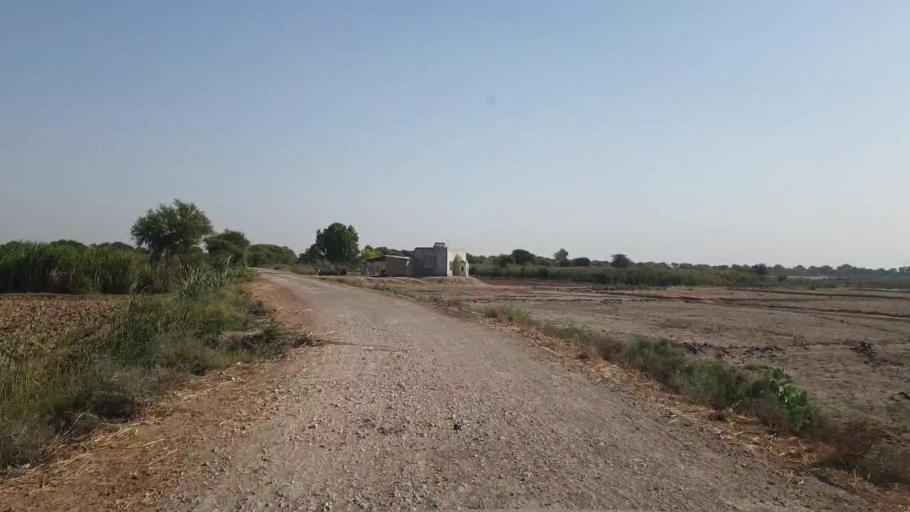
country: PK
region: Sindh
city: Matli
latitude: 25.0198
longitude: 68.7385
